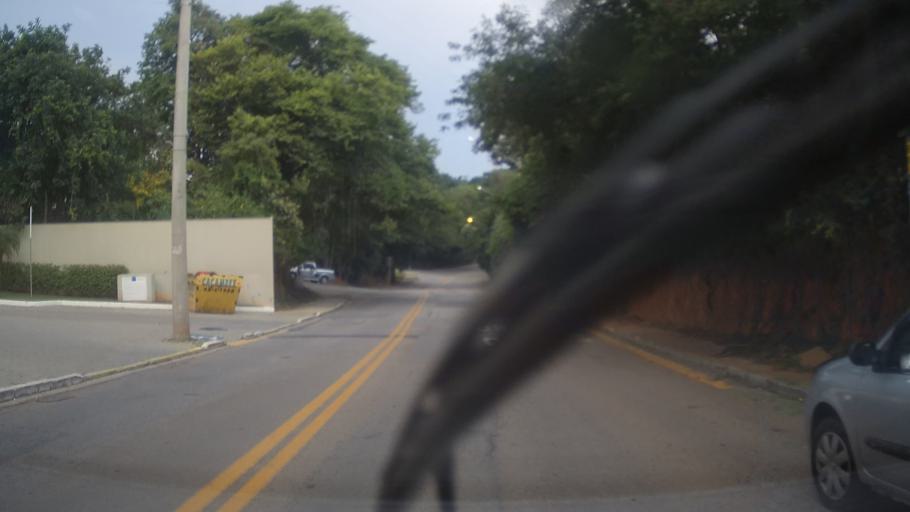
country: BR
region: Sao Paulo
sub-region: Itupeva
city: Itupeva
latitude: -23.1840
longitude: -46.9892
